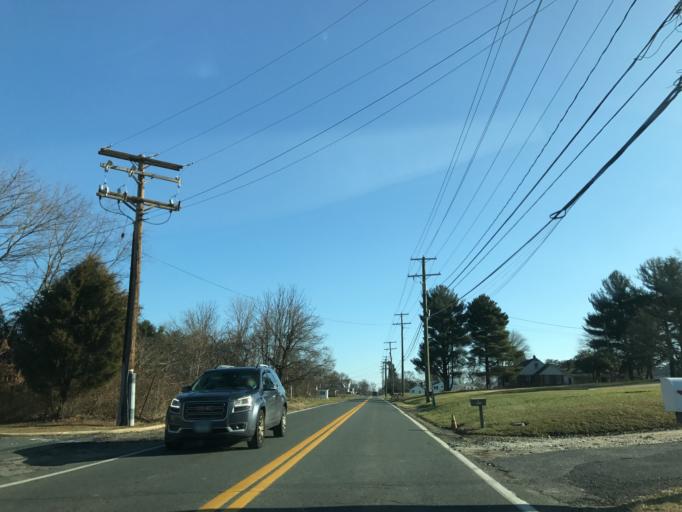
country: US
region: Maryland
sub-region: Baltimore County
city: White Marsh
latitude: 39.3671
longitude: -76.4051
